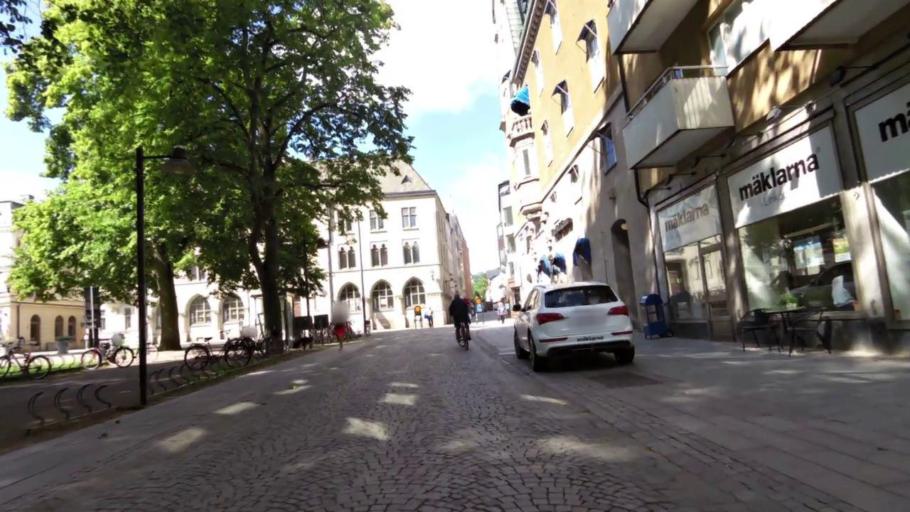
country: SE
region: OEstergoetland
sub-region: Linkopings Kommun
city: Linkoping
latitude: 58.4118
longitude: 15.6251
